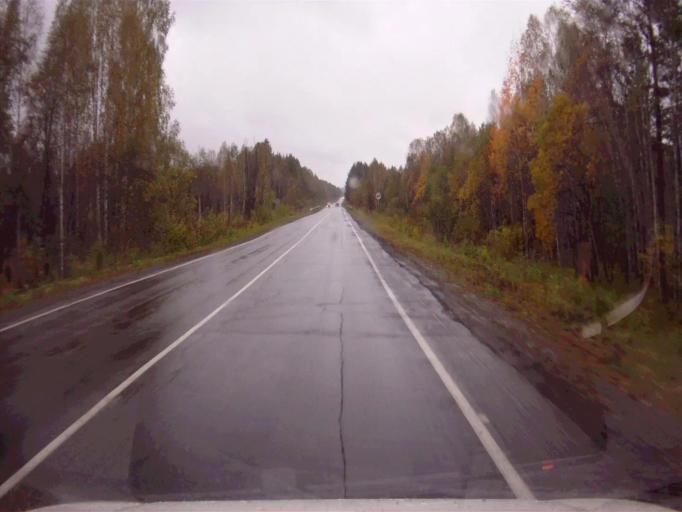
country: RU
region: Chelyabinsk
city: Verkhniy Ufaley
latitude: 55.9722
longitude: 60.3561
